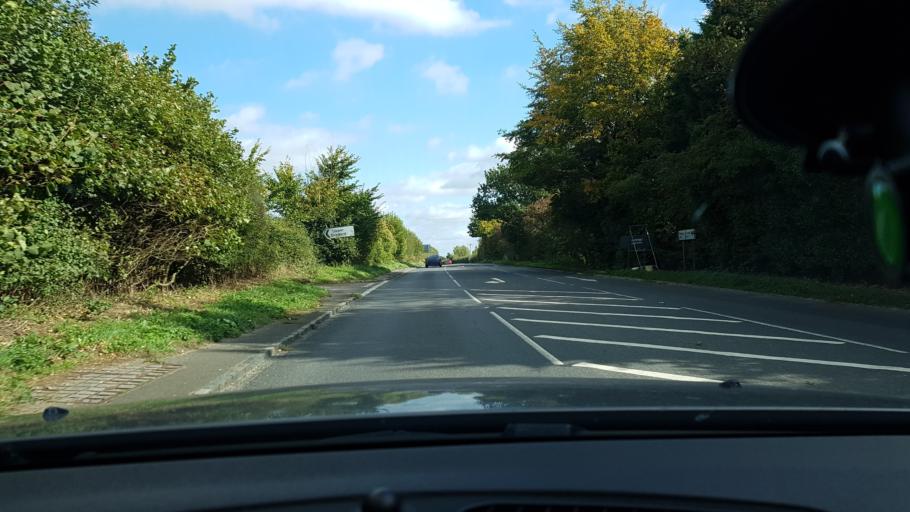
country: GB
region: England
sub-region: West Berkshire
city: Hungerford
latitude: 51.4158
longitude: -1.4940
